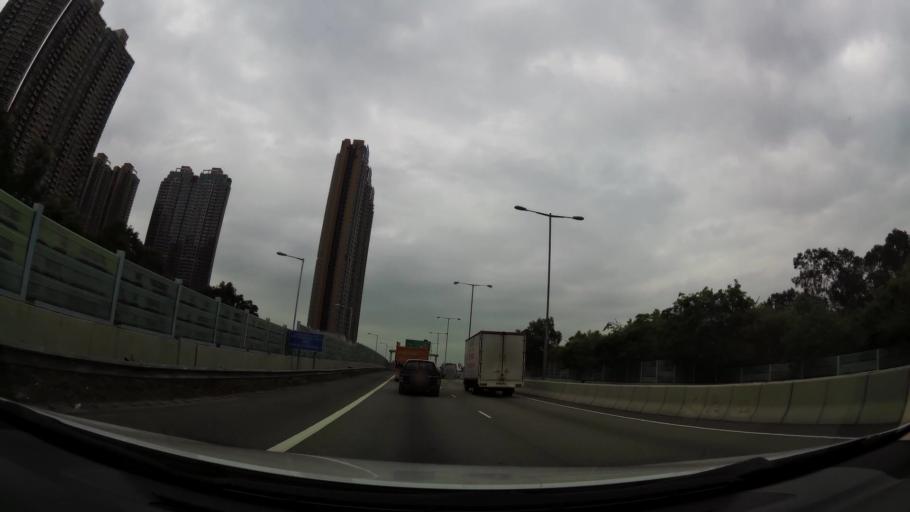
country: HK
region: Yuen Long
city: Yuen Long Kau Hui
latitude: 22.4425
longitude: 114.0393
